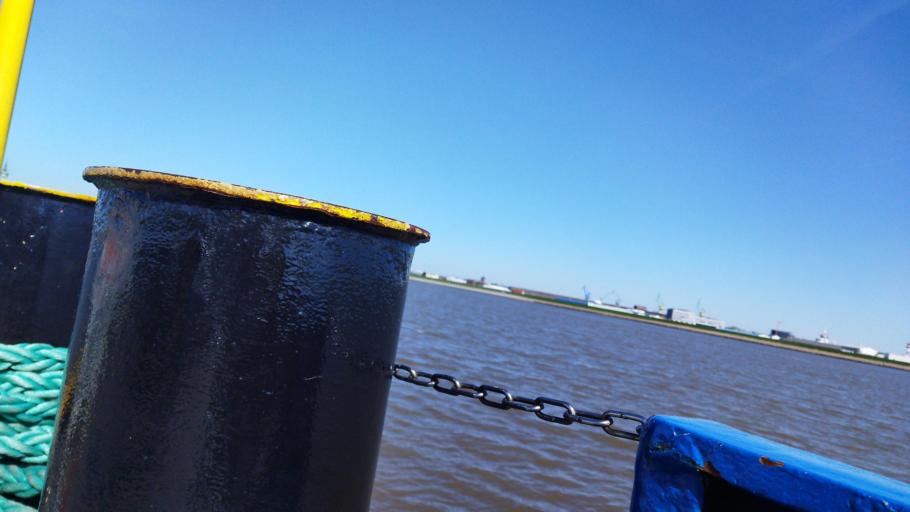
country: DE
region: Bremen
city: Bremerhaven
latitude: 53.5255
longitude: 8.5625
